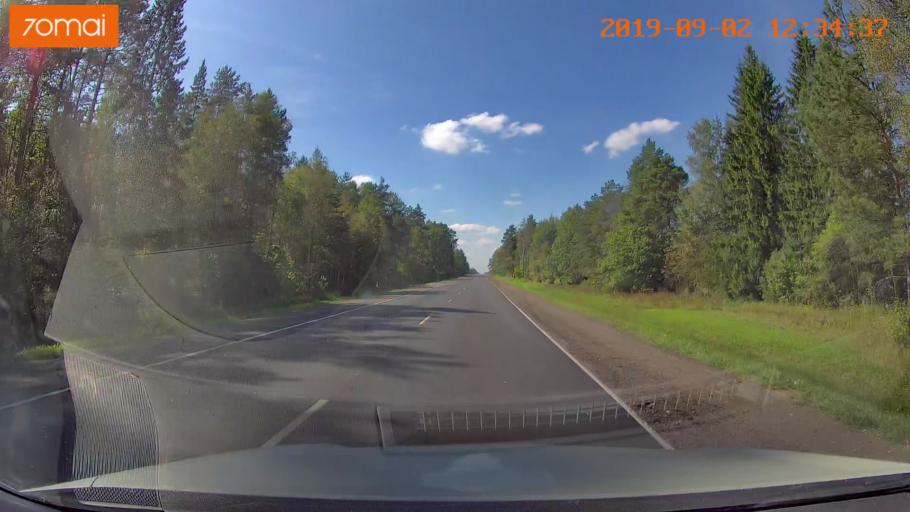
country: RU
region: Smolensk
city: Shumyachi
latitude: 53.8090
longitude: 32.4000
